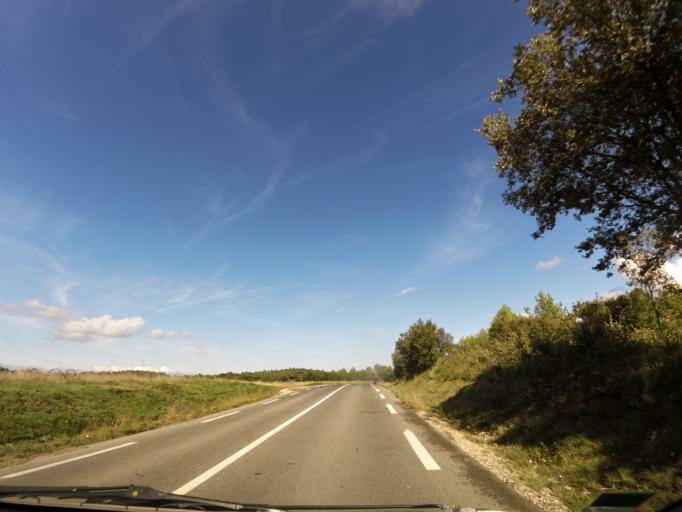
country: FR
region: Languedoc-Roussillon
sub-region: Departement du Gard
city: Villevieille
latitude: 43.8573
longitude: 4.0970
